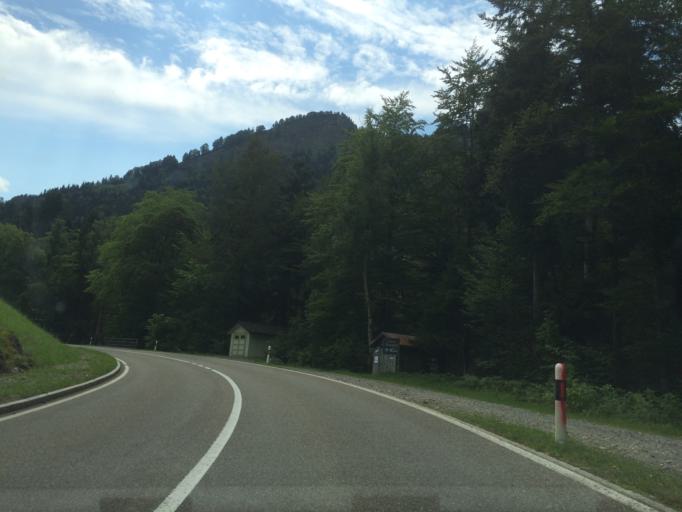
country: CH
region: Appenzell Ausserrhoden
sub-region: Bezirk Hinterland
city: Urnasch
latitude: 47.2812
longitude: 9.2775
